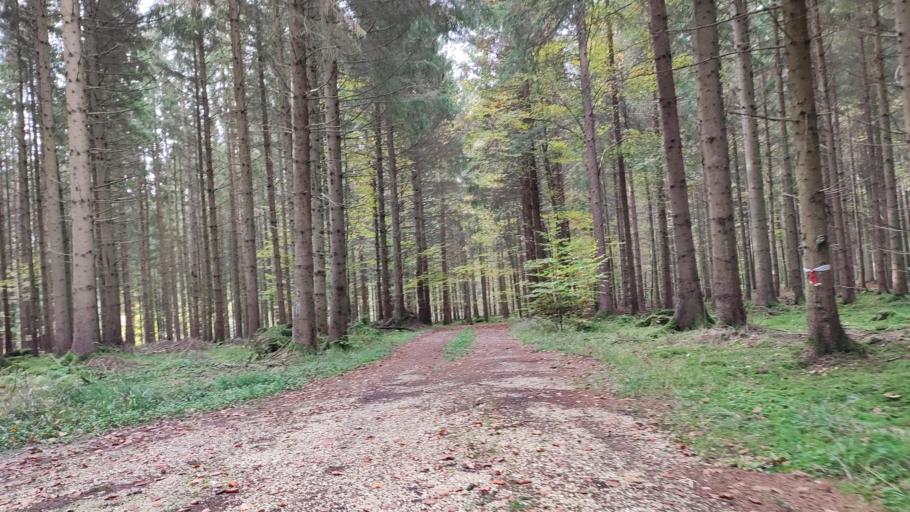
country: DE
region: Bavaria
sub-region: Swabia
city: Ziemetshausen
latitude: 48.3305
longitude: 10.5218
